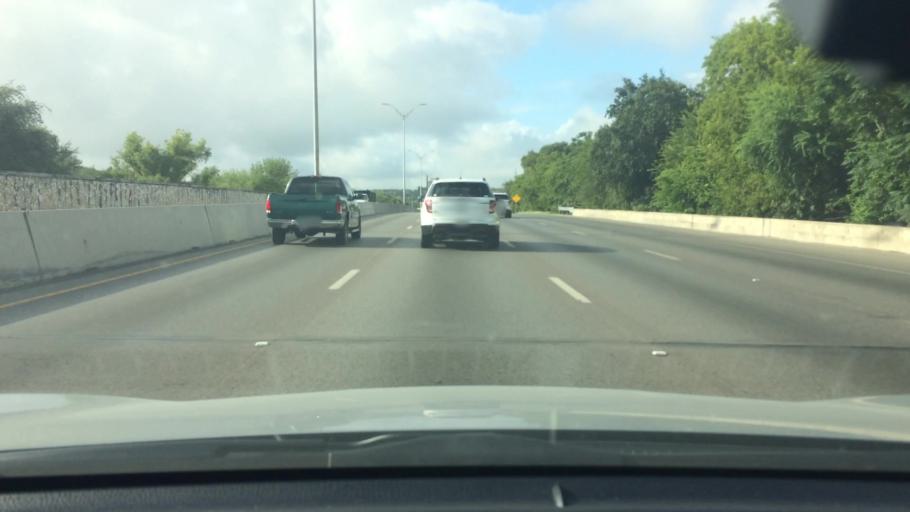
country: US
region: Texas
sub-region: Bexar County
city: Olmos Park
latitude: 29.4822
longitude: -98.4819
